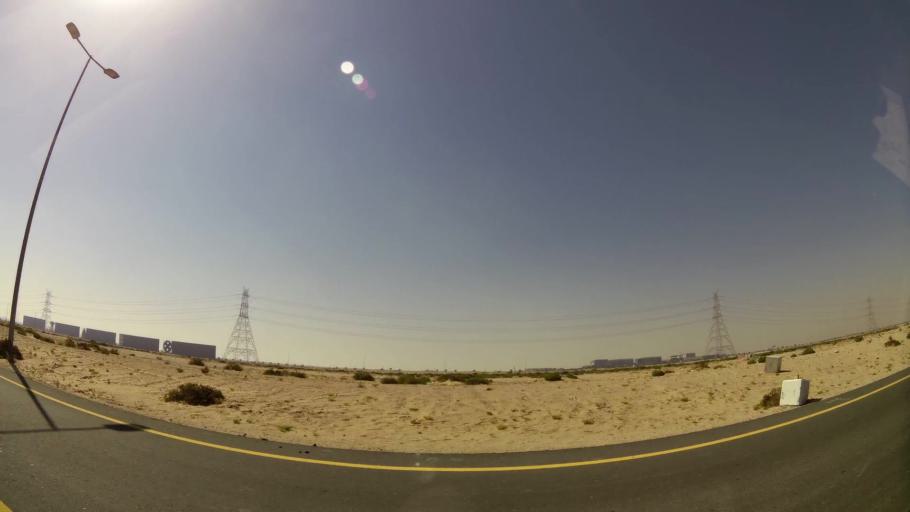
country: AE
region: Dubai
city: Dubai
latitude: 24.9052
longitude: 55.0683
